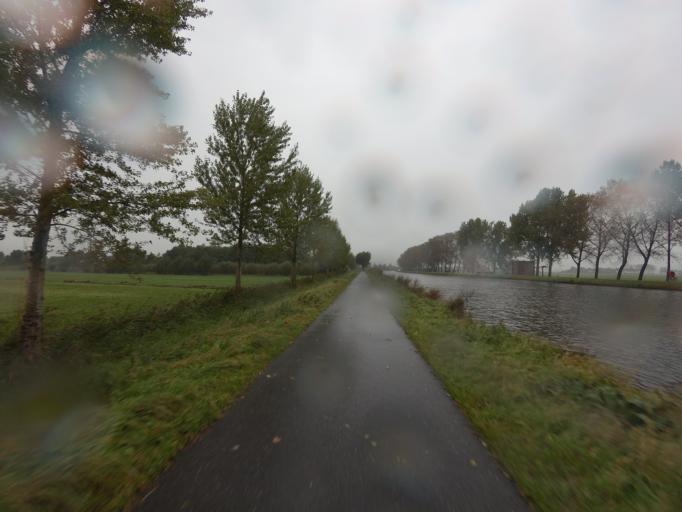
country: NL
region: South Holland
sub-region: Gemeente Leerdam
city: Leerdam
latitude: 51.9321
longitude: 5.0343
